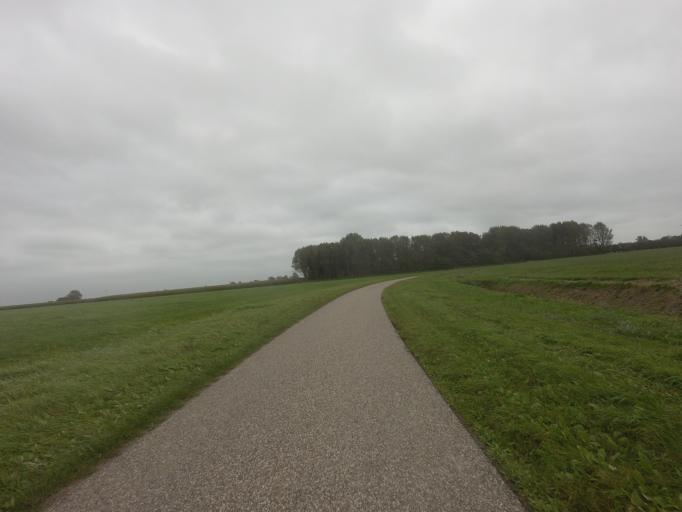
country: NL
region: Friesland
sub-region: Gemeente Ferwerderadiel
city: Ferwert
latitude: 53.3385
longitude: 5.8572
